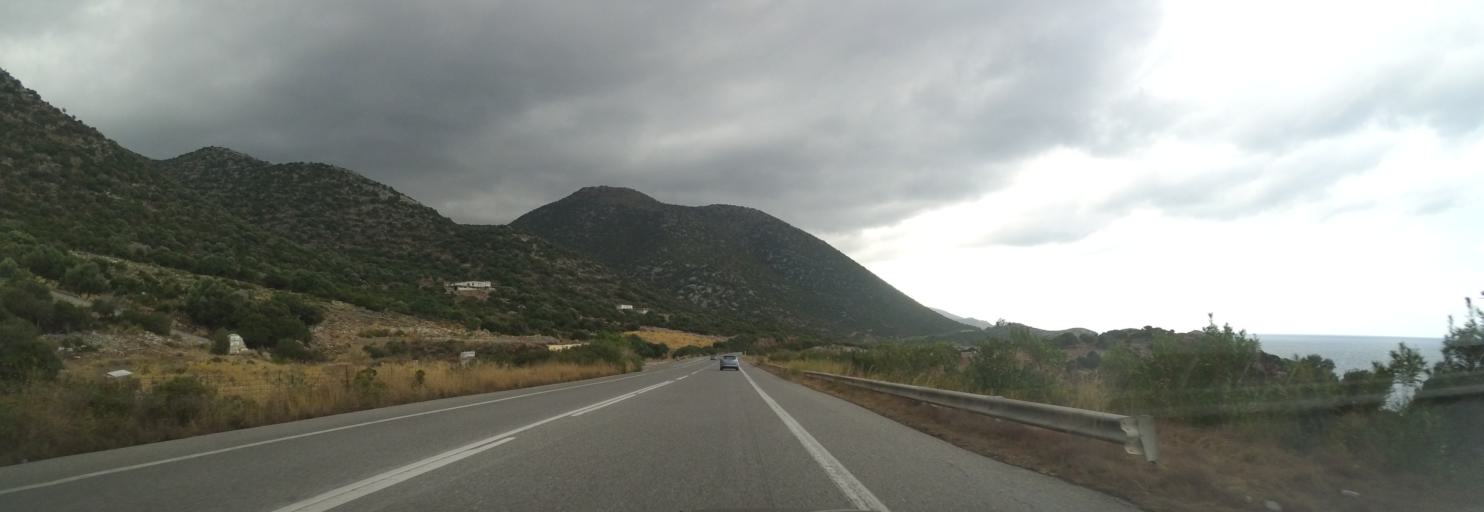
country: GR
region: Crete
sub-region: Nomos Rethymnis
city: Zoniana
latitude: 35.4052
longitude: 24.8479
